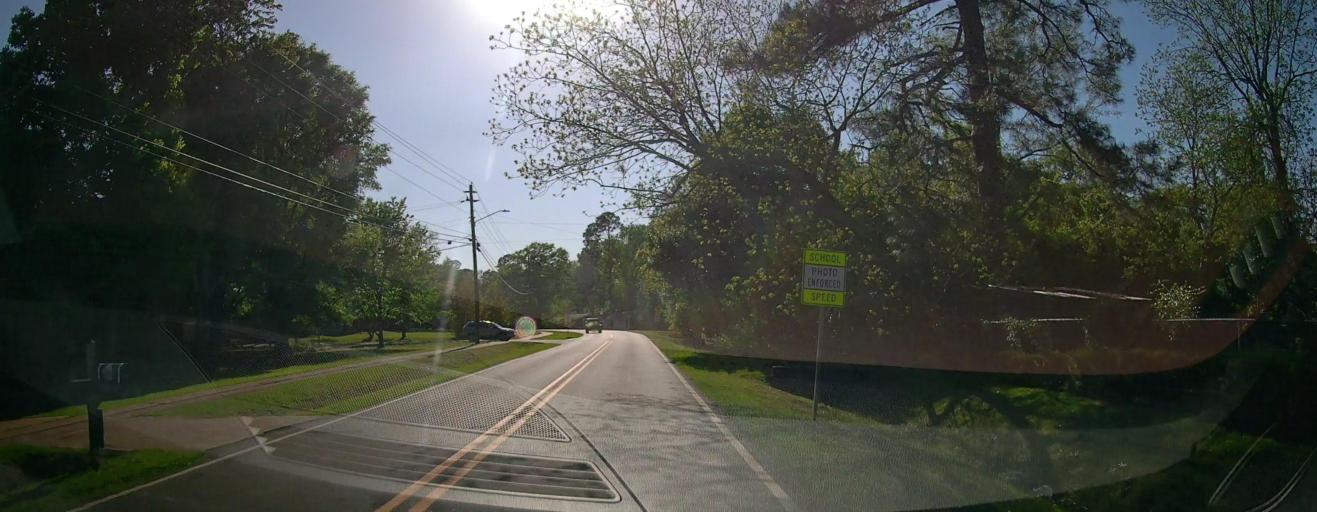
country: US
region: Georgia
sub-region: Houston County
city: Perry
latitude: 32.4508
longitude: -83.7189
